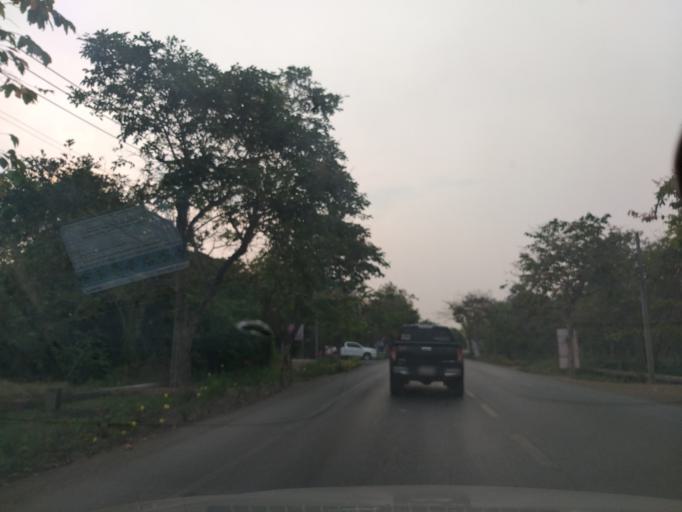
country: TH
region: Bangkok
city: Nong Chok
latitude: 13.8463
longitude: 100.8941
